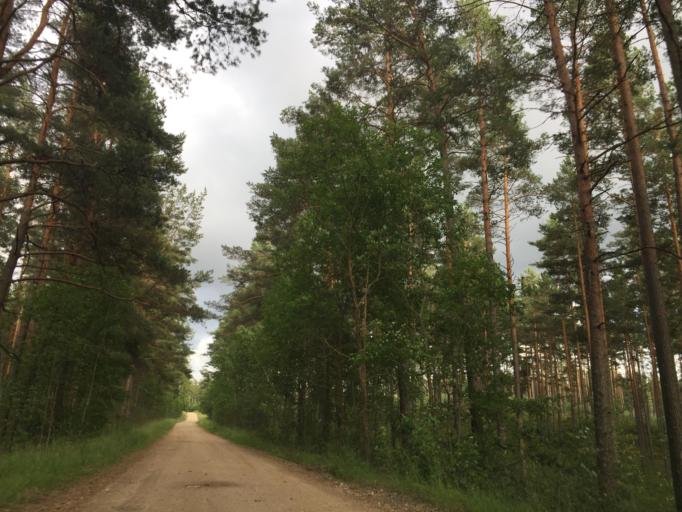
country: LV
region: Carnikava
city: Carnikava
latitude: 57.1716
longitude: 24.3536
